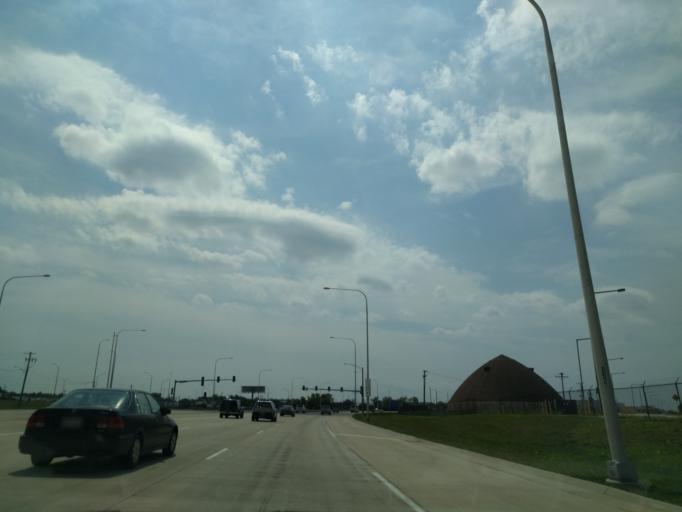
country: US
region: Illinois
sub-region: Cook County
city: Schiller Park
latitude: 41.9669
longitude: -87.8765
